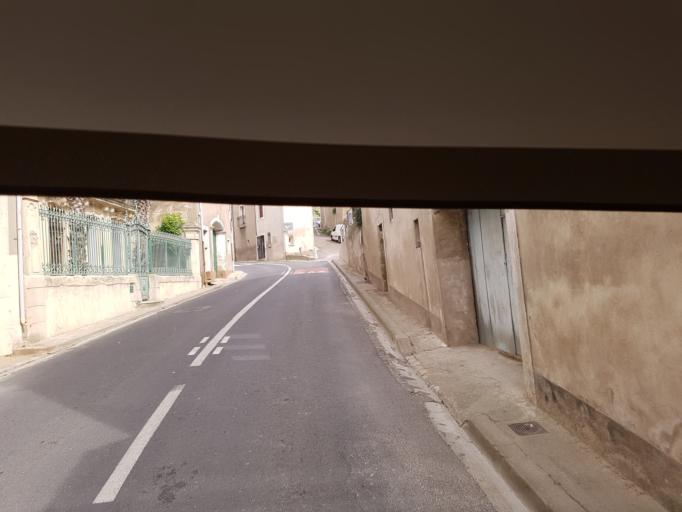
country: FR
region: Languedoc-Roussillon
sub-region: Departement de l'Herault
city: Lespignan
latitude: 43.2744
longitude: 3.1737
